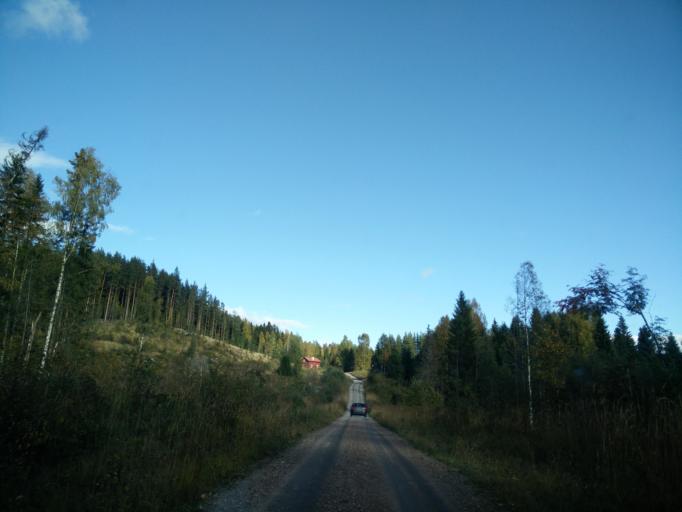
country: SE
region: Vaesternorrland
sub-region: Sundsvalls Kommun
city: Matfors
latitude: 62.3308
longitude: 16.9171
